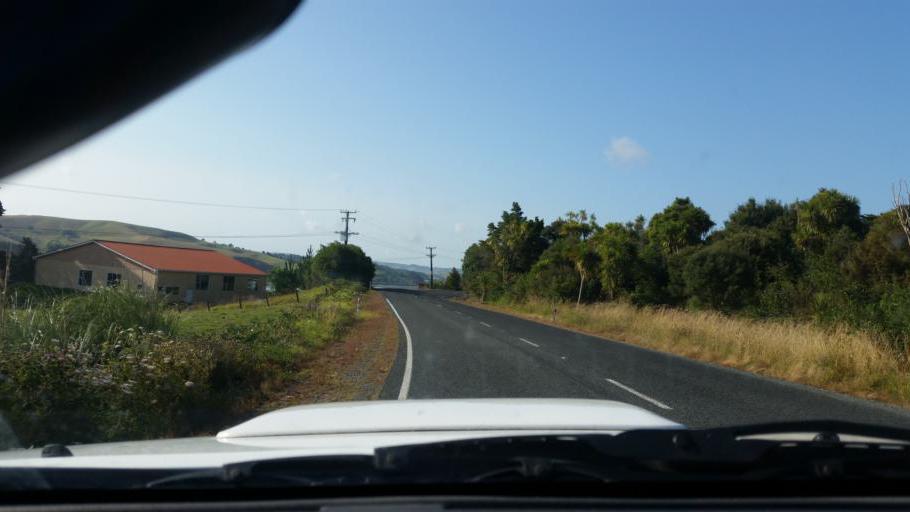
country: NZ
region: Northland
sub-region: Whangarei
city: Ruakaka
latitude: -36.1285
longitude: 174.2299
